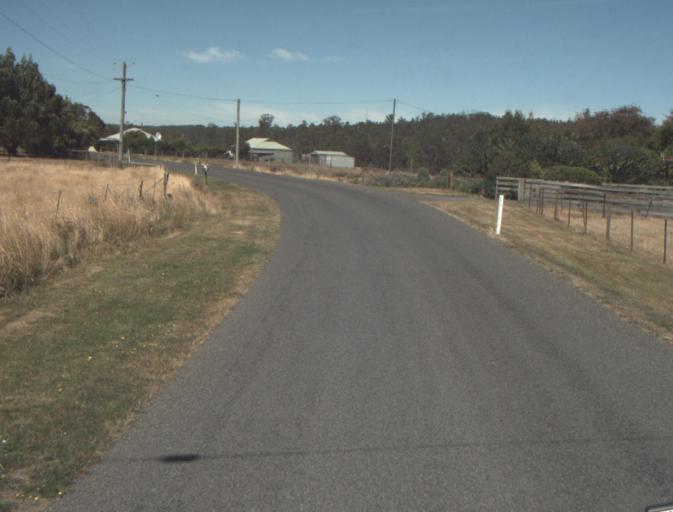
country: AU
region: Tasmania
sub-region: Launceston
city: Newstead
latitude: -41.3754
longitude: 147.2964
